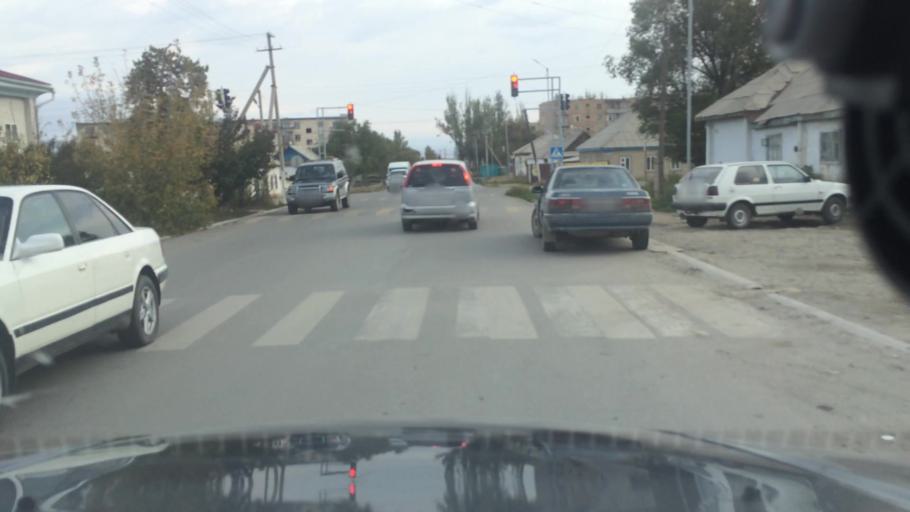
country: KG
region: Ysyk-Koel
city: Karakol
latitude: 42.4943
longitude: 78.3893
